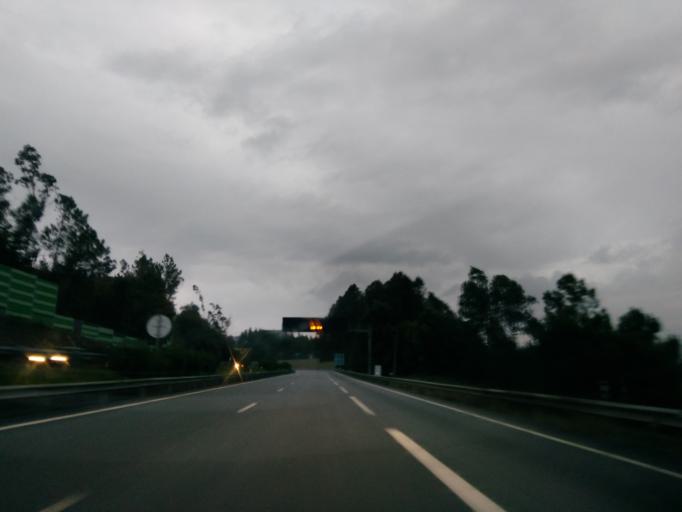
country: PT
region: Braga
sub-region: Vila Nova de Famalicao
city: Vila Nova de Famalicao
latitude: 41.4411
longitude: -8.4934
